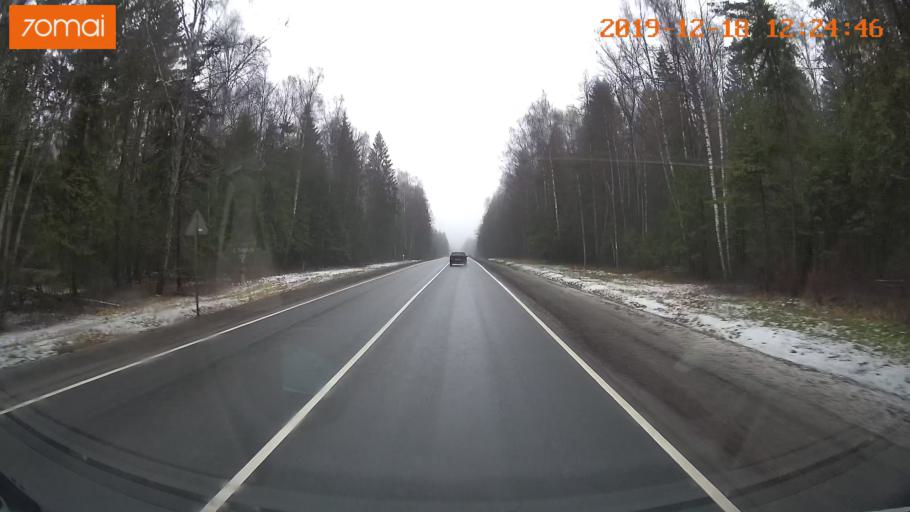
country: RU
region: Moskovskaya
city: Novopetrovskoye
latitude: 56.0291
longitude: 36.5006
